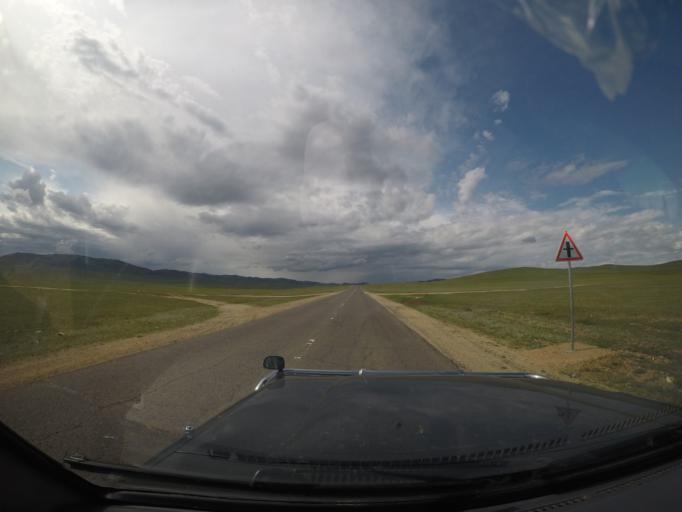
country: MN
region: Hentiy
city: Modot
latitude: 47.6217
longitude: 109.1787
